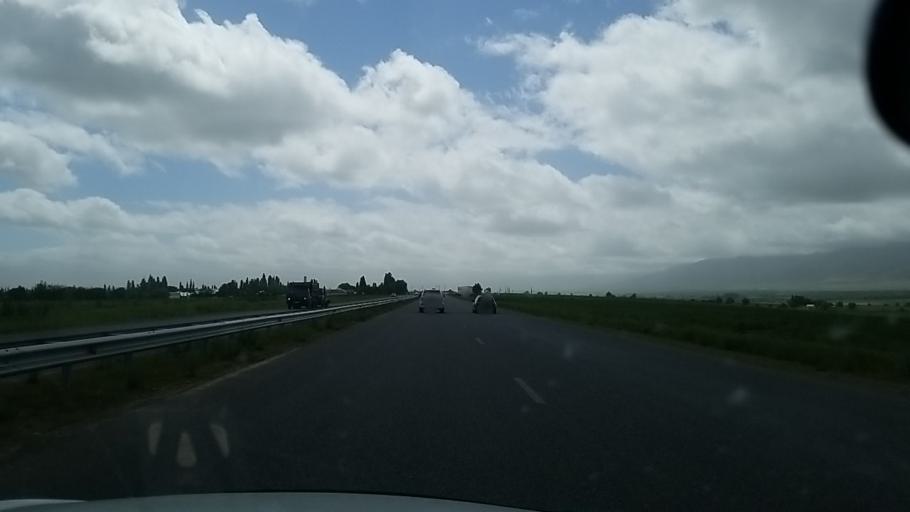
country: KZ
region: Ongtustik Qazaqstan
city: Kokterek
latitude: 42.5331
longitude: 70.2967
